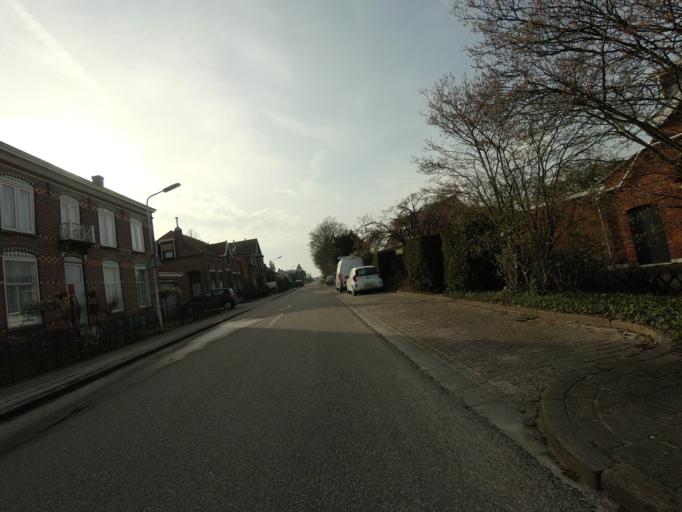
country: NL
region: Zeeland
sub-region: Gemeente Terneuzen
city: Zaamslag
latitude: 51.3879
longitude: 3.9796
